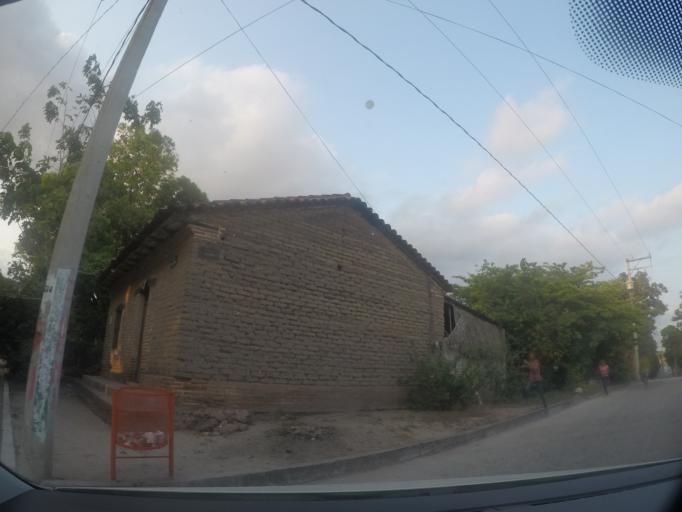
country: MX
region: Oaxaca
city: San Jeronimo Ixtepec
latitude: 16.5853
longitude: -95.2089
